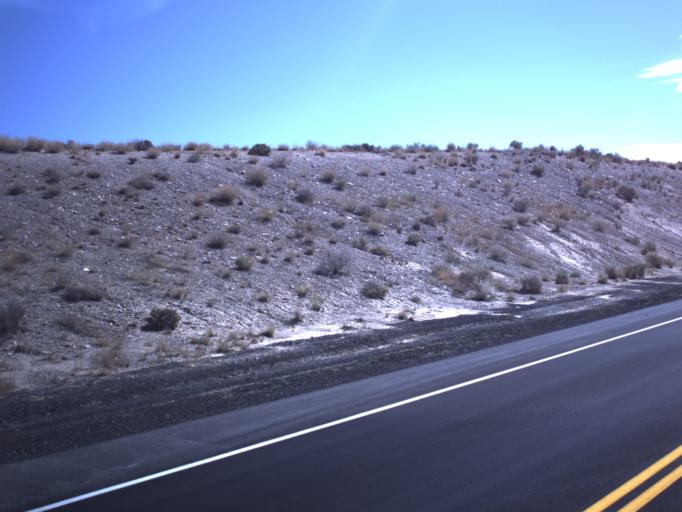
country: US
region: Utah
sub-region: Utah County
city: Eagle Mountain
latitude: 40.0686
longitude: -112.3279
